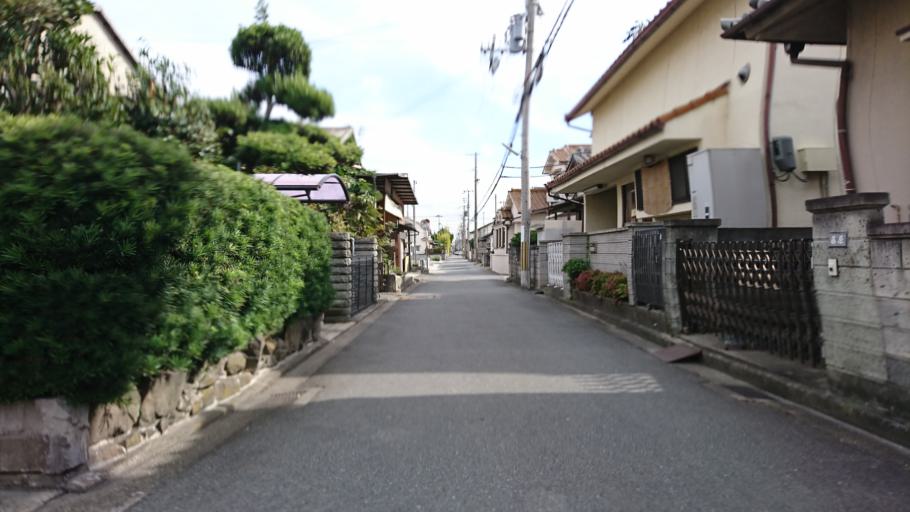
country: JP
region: Hyogo
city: Kakogawacho-honmachi
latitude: 34.7440
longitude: 134.8139
